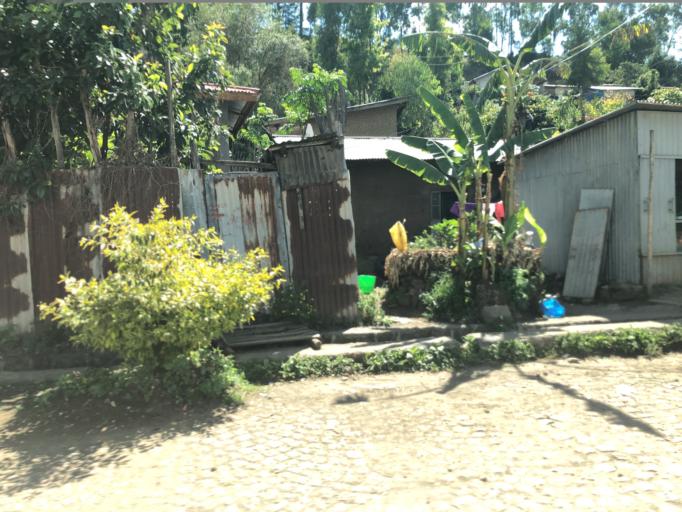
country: ET
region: Amhara
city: Lalibela
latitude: 12.0345
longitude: 39.0496
